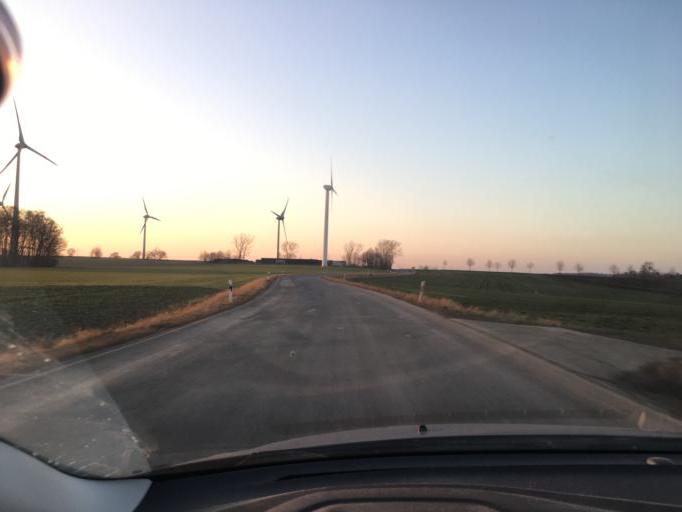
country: DE
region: Saxony
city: Lunzenau
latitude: 50.9797
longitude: 12.7303
